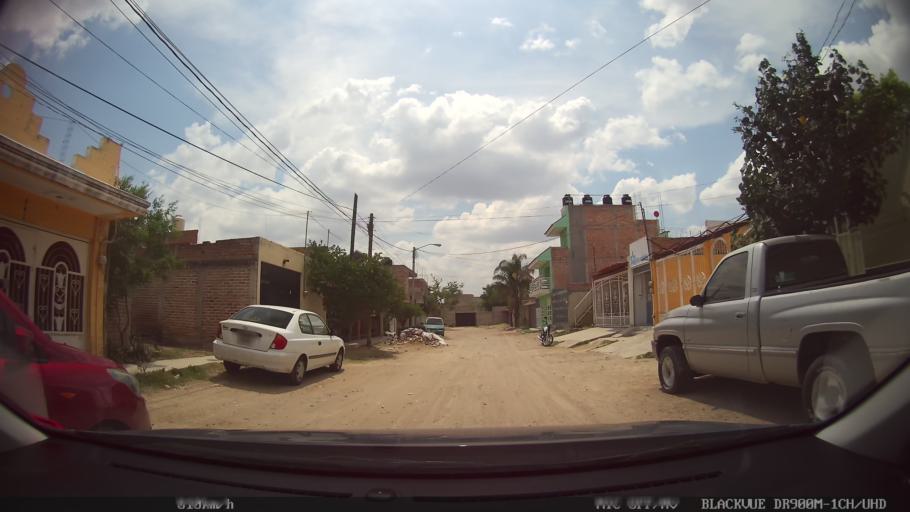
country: MX
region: Jalisco
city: Tonala
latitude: 20.6821
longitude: -103.2378
